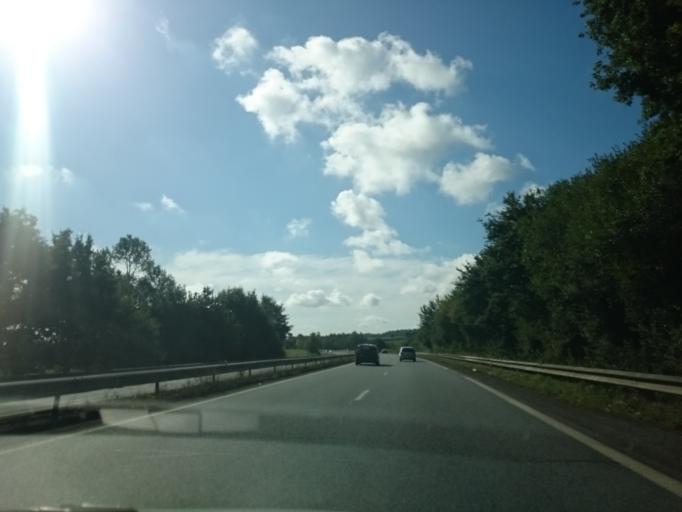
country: FR
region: Brittany
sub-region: Departement des Cotes-d'Armor
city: Broons
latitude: 48.2994
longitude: -2.2315
